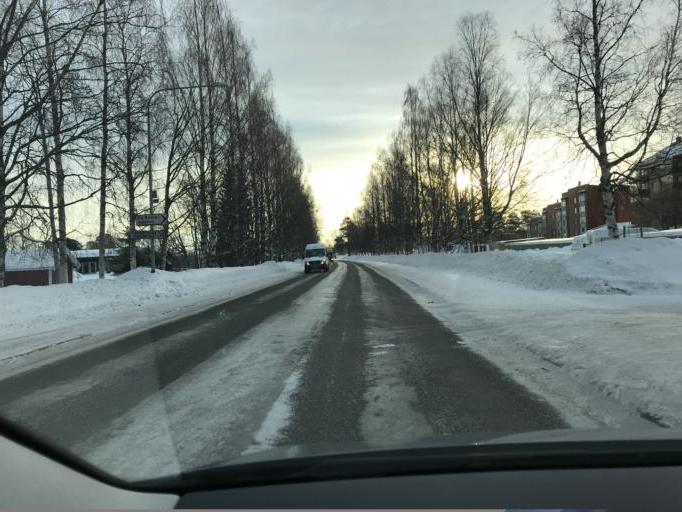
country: SE
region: Norrbotten
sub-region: Lulea Kommun
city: Bergnaset
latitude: 65.6053
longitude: 22.1141
